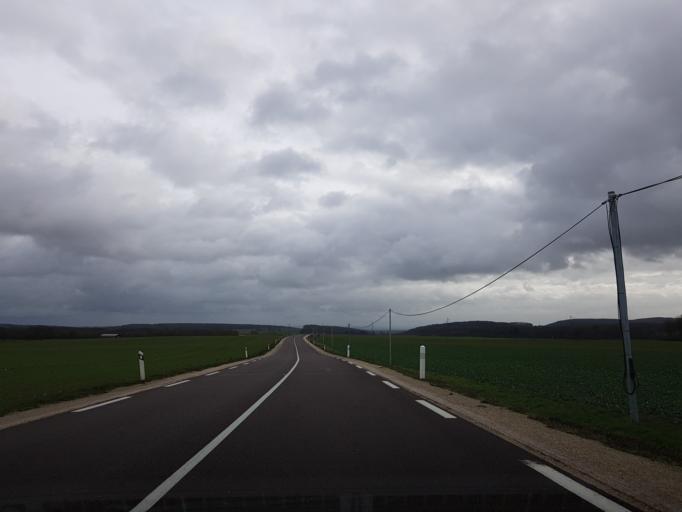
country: FR
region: Champagne-Ardenne
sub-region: Departement de la Haute-Marne
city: Fayl-Billot
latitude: 47.7632
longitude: 5.7122
